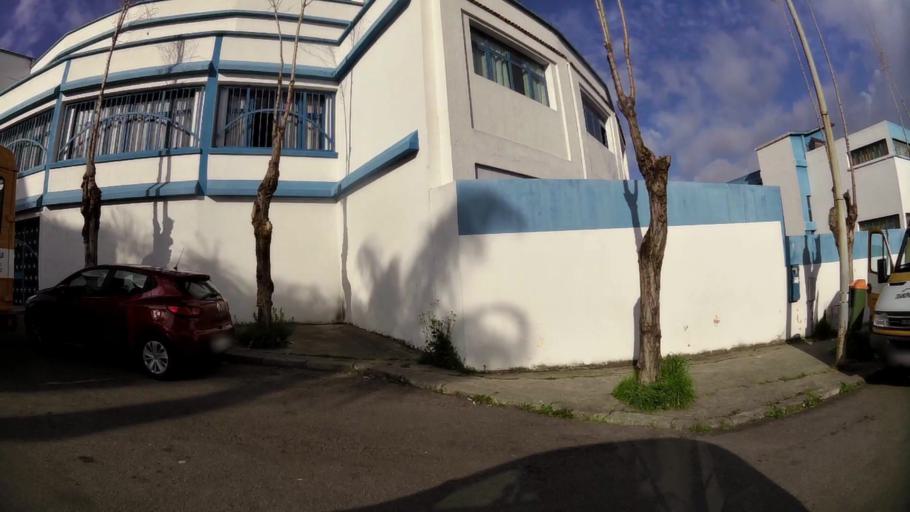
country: MA
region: Tanger-Tetouan
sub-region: Tanger-Assilah
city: Tangier
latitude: 35.7700
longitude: -5.7964
